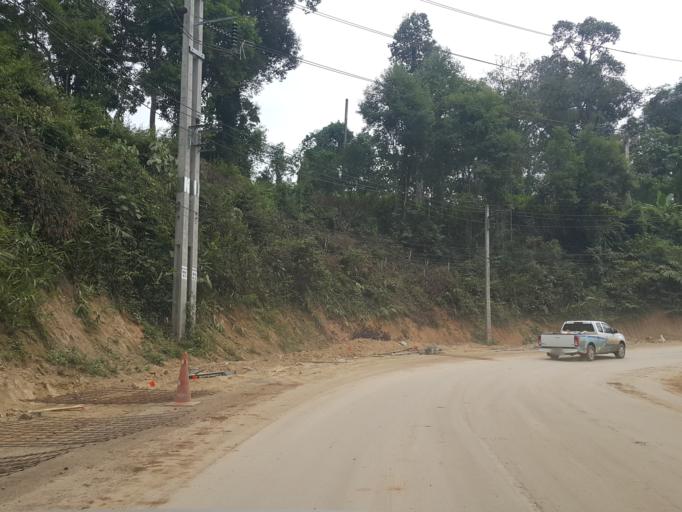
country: TH
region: Chiang Mai
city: Mae Taeng
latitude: 19.1438
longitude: 98.6977
